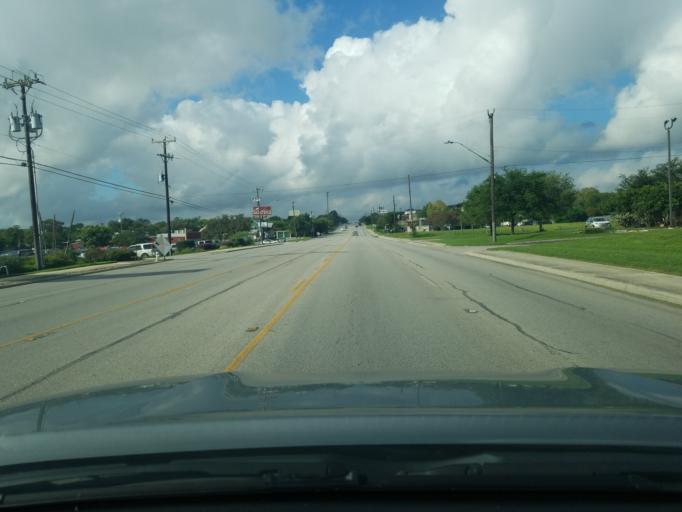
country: US
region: Texas
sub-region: Bexar County
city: Live Oak
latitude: 29.5888
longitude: -98.3576
